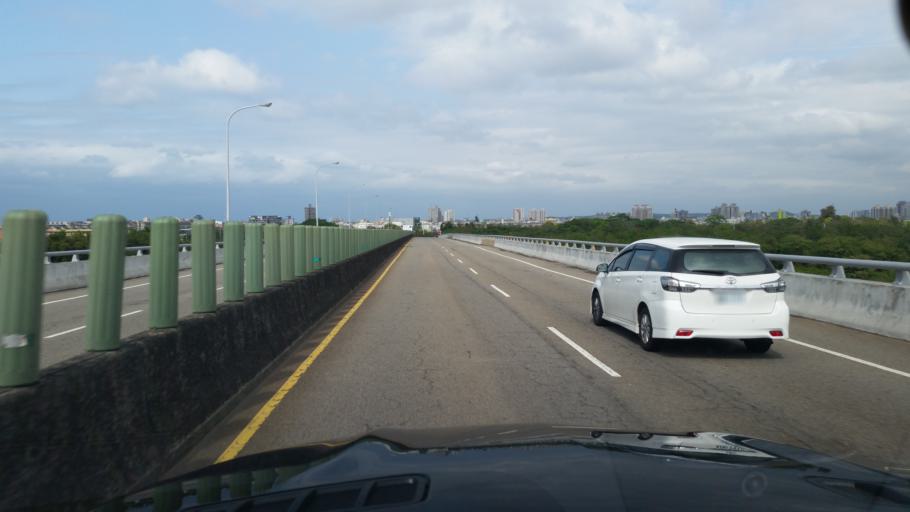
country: TW
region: Taiwan
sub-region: Miaoli
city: Miaoli
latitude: 24.6654
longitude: 120.8671
